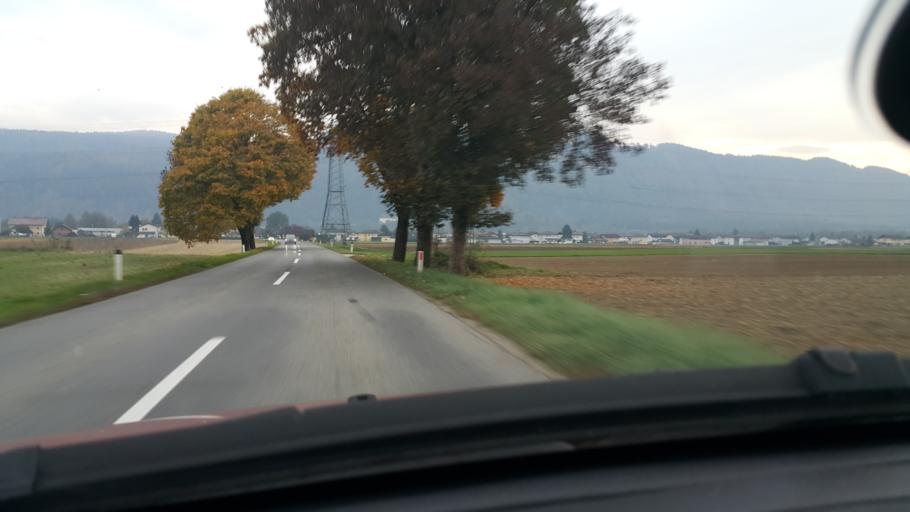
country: AT
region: Carinthia
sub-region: Politischer Bezirk Klagenfurt Land
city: Ebenthal
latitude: 46.6158
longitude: 14.3983
